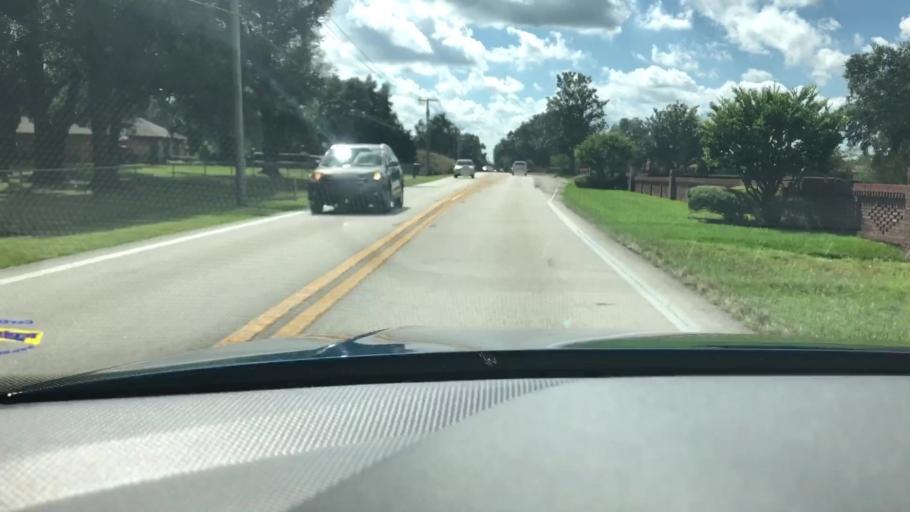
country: US
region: Florida
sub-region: Polk County
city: Gibsonia
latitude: 28.1393
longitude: -81.9384
